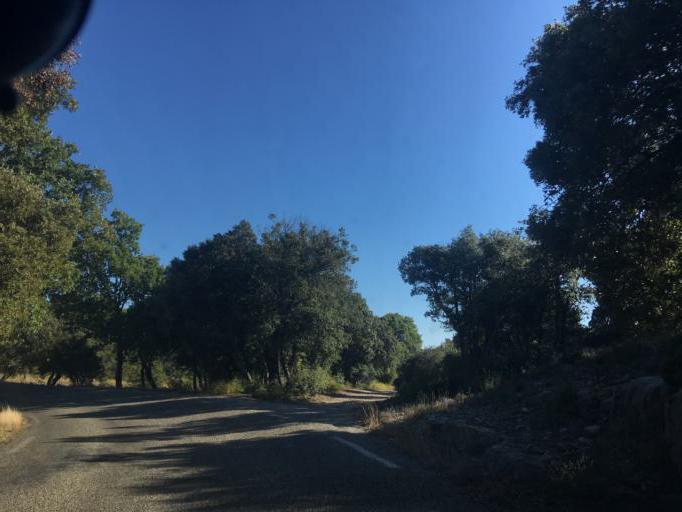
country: FR
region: Provence-Alpes-Cote d'Azur
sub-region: Departement du Var
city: Regusse
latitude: 43.7263
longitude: 6.1255
